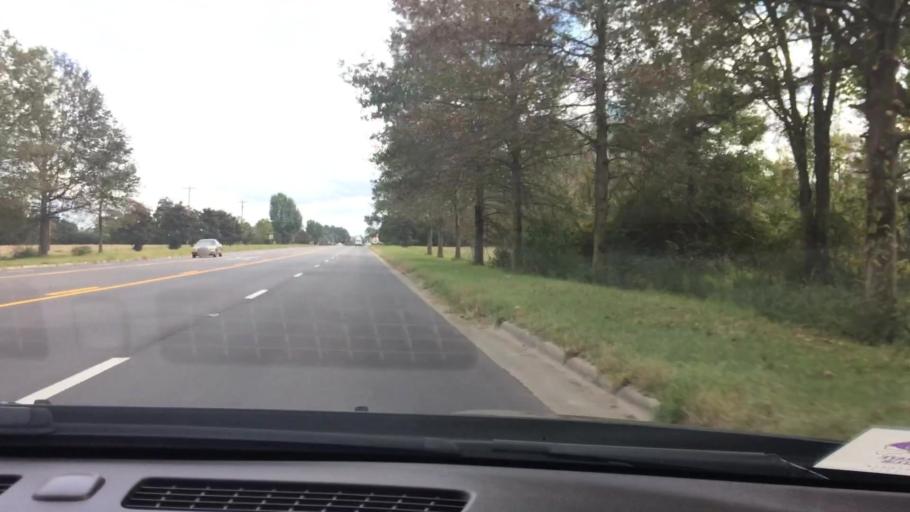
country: US
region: North Carolina
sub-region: Pitt County
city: Farmville
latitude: 35.5849
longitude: -77.6009
